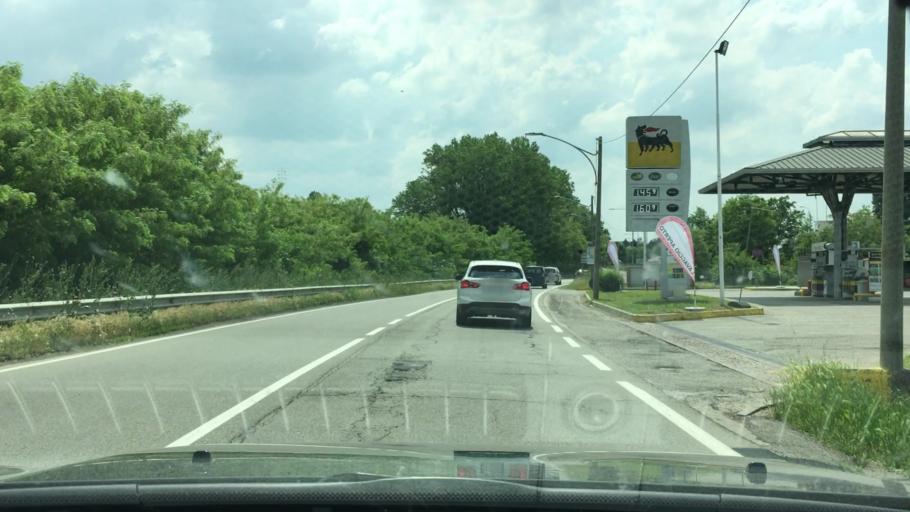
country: IT
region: Emilia-Romagna
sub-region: Provincia di Bologna
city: Progresso
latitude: 44.5374
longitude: 11.3696
